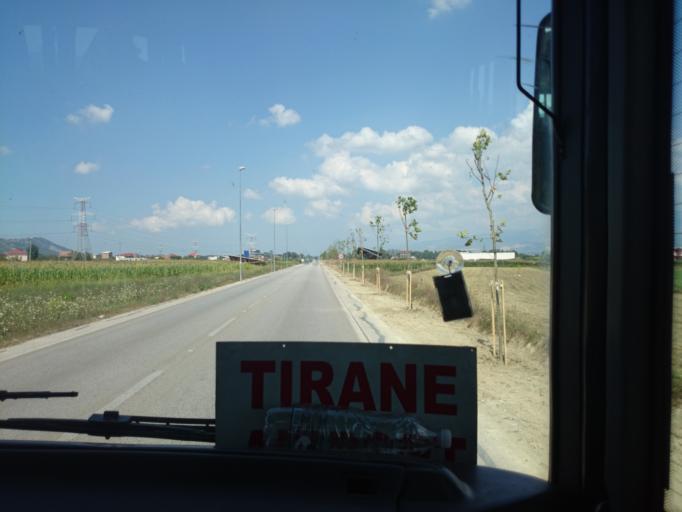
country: AL
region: Tirane
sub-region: Rrethi i Tiranes
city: Berxull
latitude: 41.3813
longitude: 19.7039
